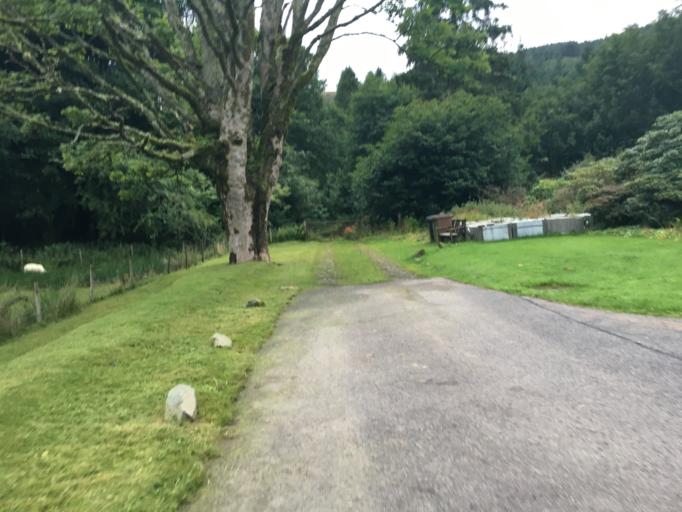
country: GB
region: Scotland
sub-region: Argyll and Bute
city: Oban
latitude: 56.2738
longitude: -5.4959
